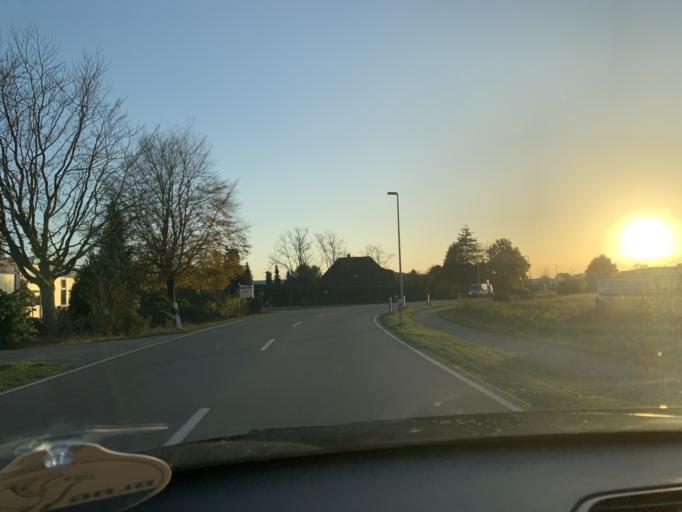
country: DE
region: Lower Saxony
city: Edewecht
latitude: 53.1225
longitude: 8.0026
